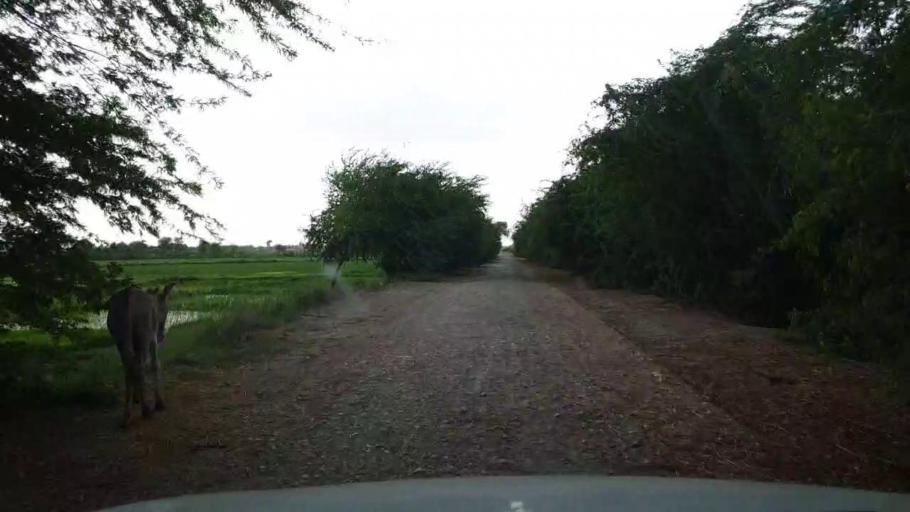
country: PK
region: Sindh
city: Kario
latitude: 24.7677
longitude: 68.5991
